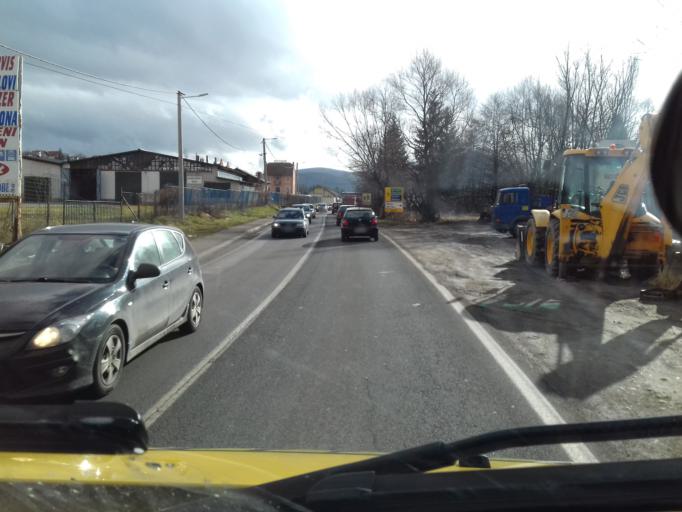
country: BA
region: Federation of Bosnia and Herzegovina
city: Travnik
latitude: 44.2205
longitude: 17.6916
